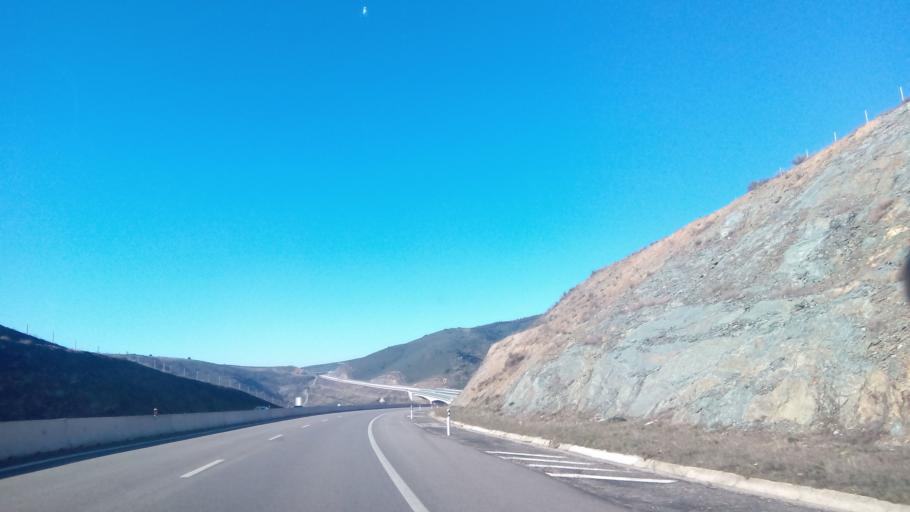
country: PT
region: Braganca
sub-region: Braganca Municipality
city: Braganca
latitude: 41.7718
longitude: -6.6710
